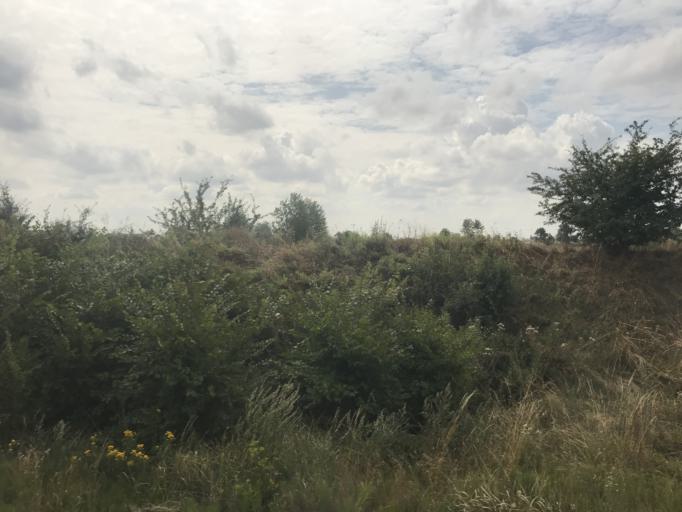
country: PL
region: Greater Poland Voivodeship
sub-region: Powiat gnieznienski
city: Gniezno
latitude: 52.5179
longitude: 17.5445
